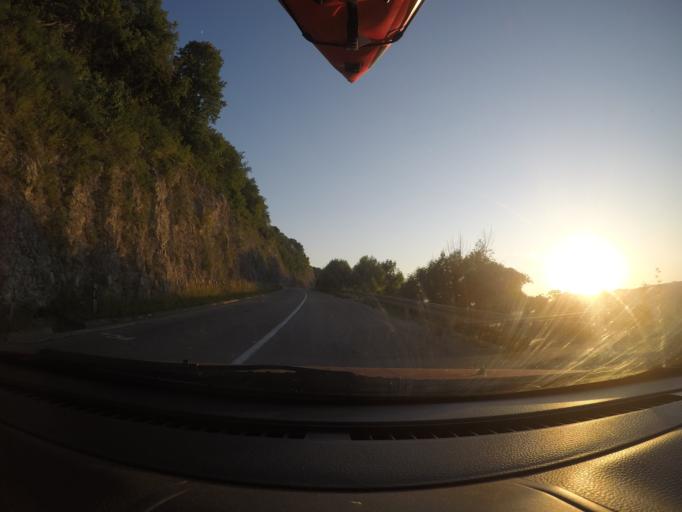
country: RO
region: Mehedinti
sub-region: Comuna Eselnita
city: Eselnita
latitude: 44.6656
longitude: 22.3418
